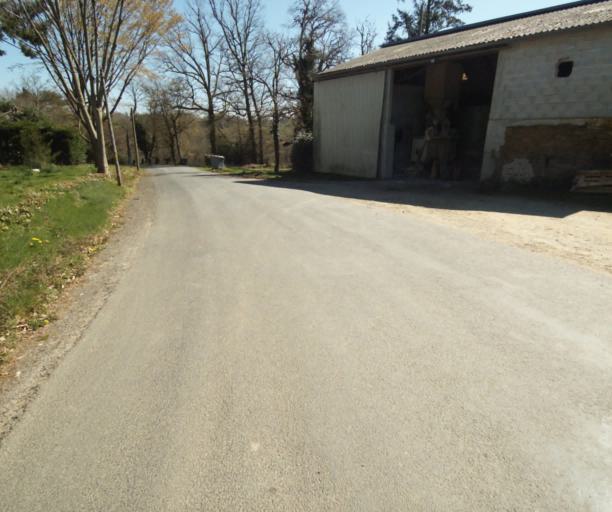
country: FR
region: Limousin
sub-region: Departement de la Correze
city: Saint-Clement
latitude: 45.3050
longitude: 1.7178
